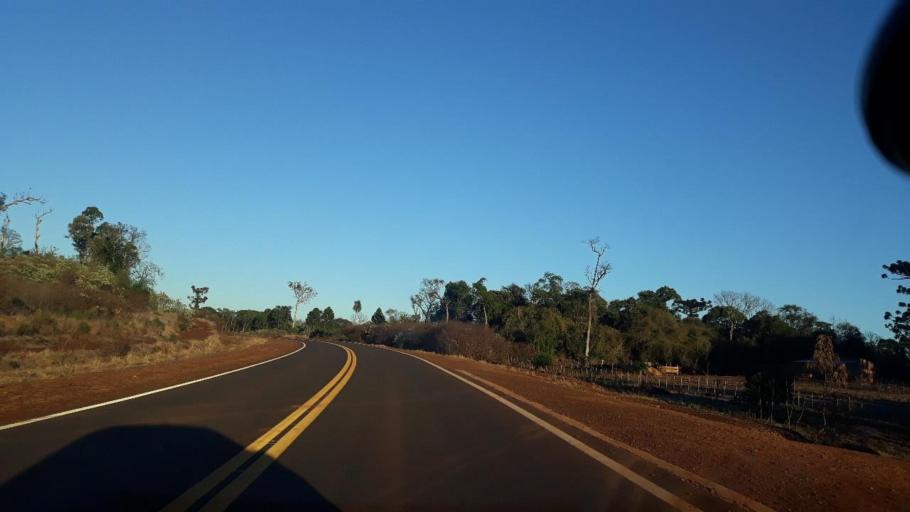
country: AR
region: Misiones
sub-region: Departamento de San Pedro
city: San Pedro
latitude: -26.5363
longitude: -53.9545
